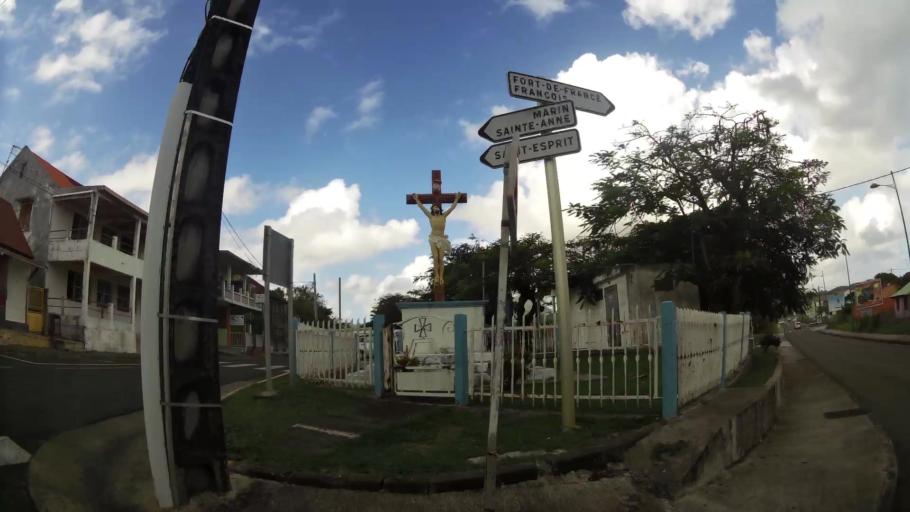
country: MQ
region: Martinique
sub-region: Martinique
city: Le Vauclin
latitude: 14.5449
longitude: -60.8423
